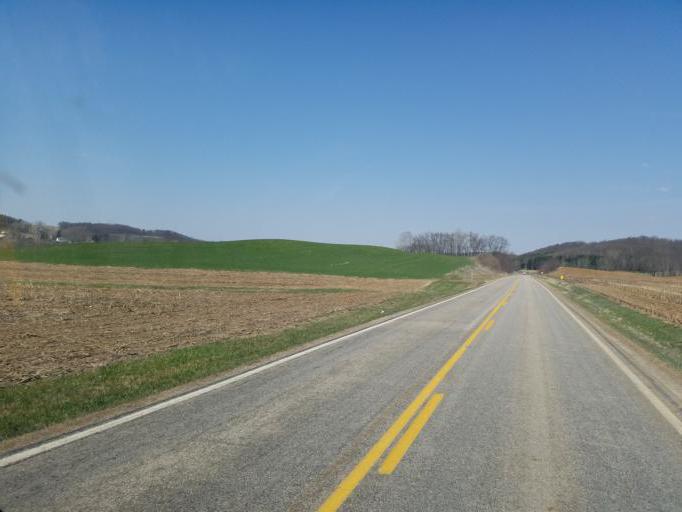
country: US
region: Ohio
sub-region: Ashland County
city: Loudonville
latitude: 40.6934
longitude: -82.1488
